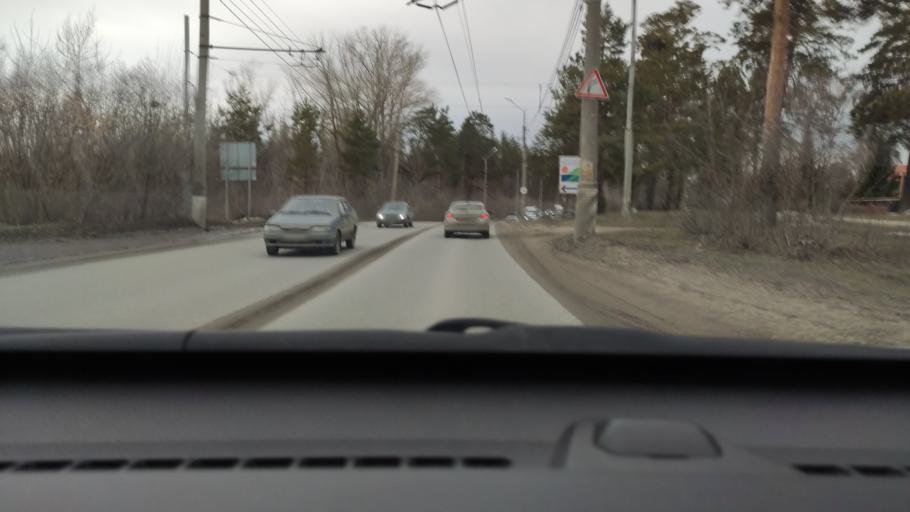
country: RU
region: Samara
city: Tol'yatti
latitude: 53.4790
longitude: 49.3619
